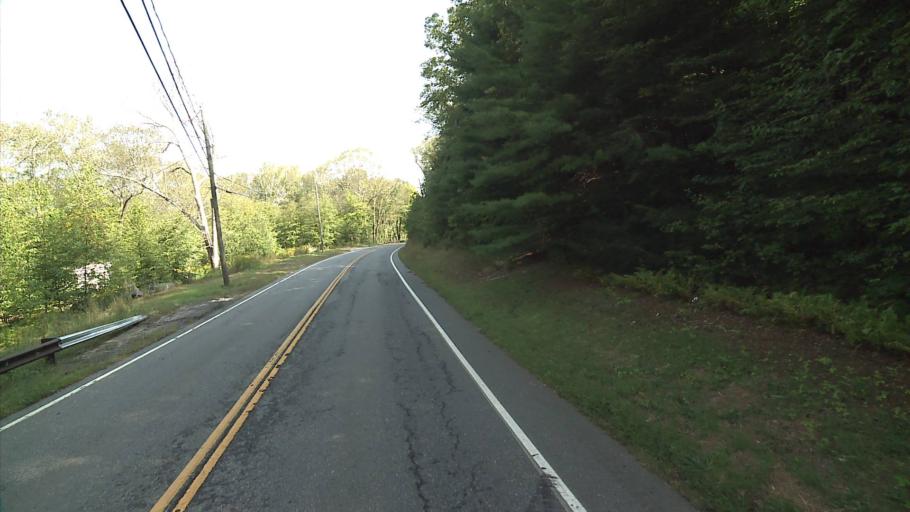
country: US
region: Connecticut
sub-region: New London County
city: Jewett City
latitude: 41.6372
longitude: -71.9948
